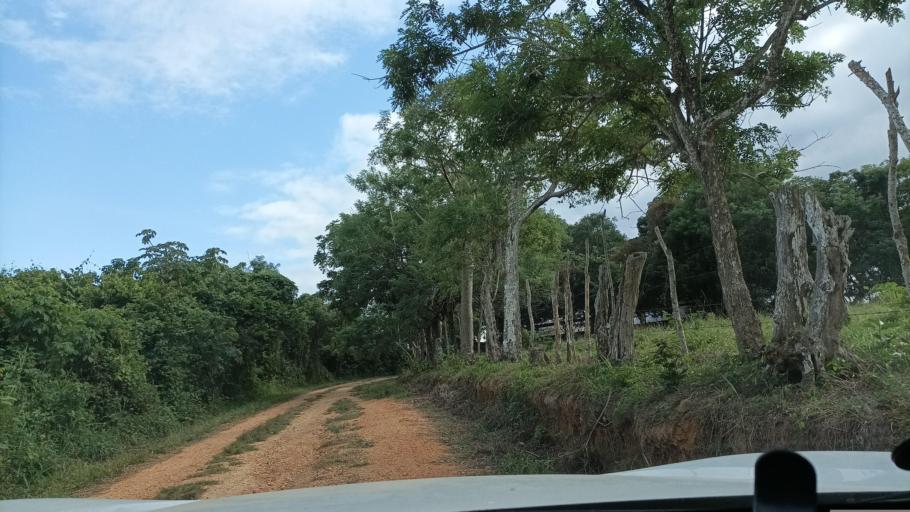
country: MX
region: Veracruz
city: Soconusco
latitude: 17.9435
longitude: -94.8823
